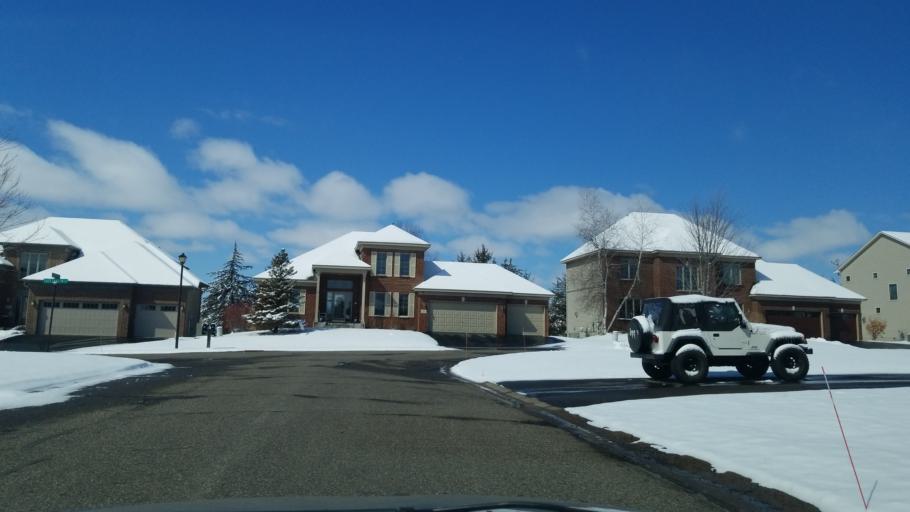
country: US
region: Wisconsin
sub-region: Saint Croix County
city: Hudson
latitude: 44.9547
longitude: -92.7018
